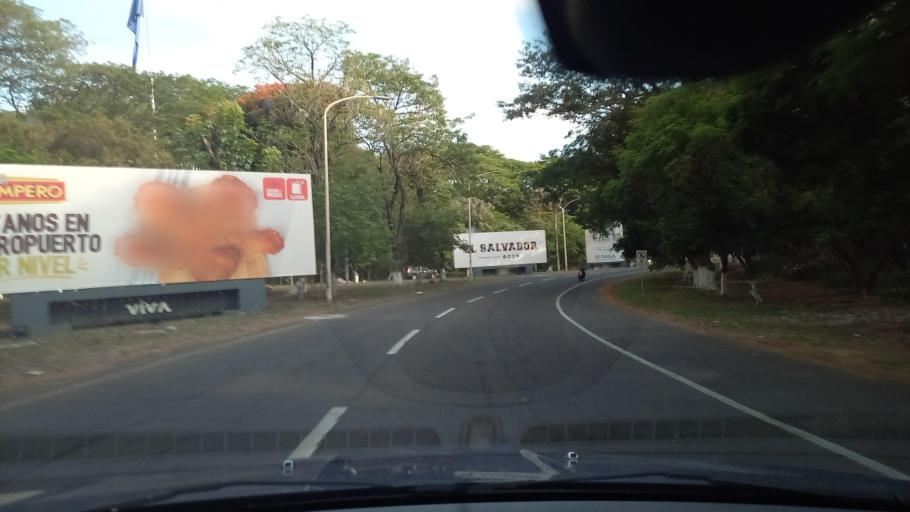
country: SV
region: La Paz
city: El Rosario
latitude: 13.4502
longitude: -89.0593
